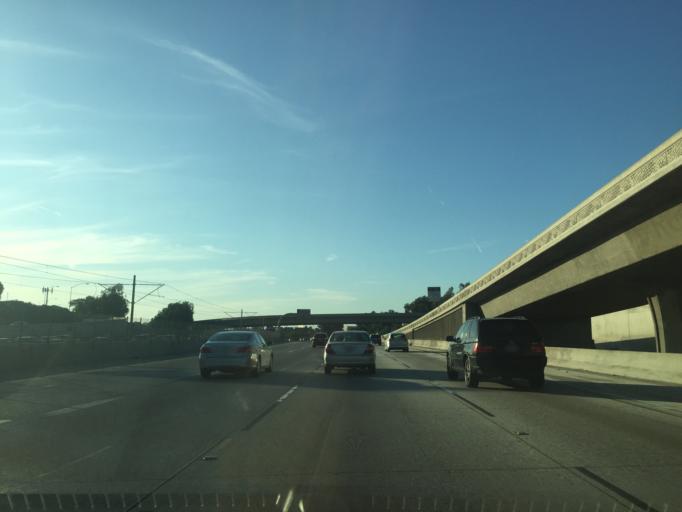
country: US
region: California
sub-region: Los Angeles County
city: Lennox
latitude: 33.9314
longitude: -118.3456
